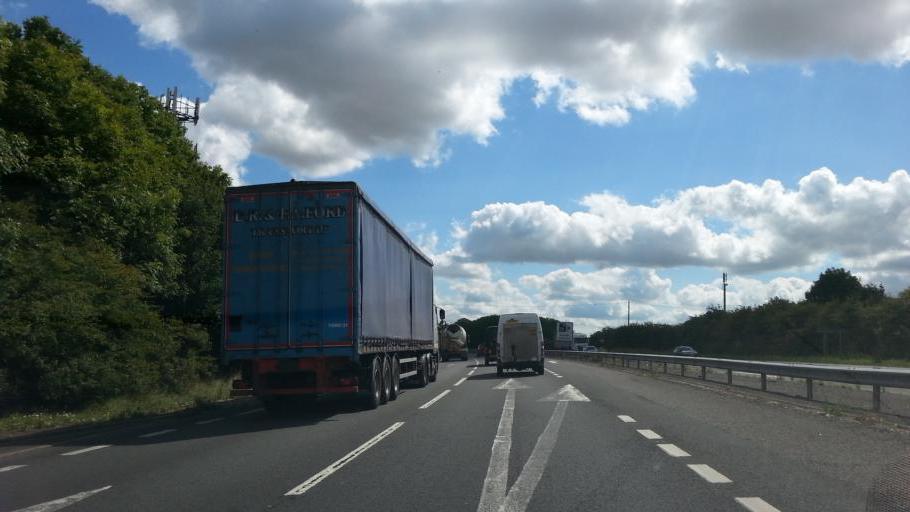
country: GB
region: England
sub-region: Northamptonshire
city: Thrapston
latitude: 52.3822
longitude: -0.4858
